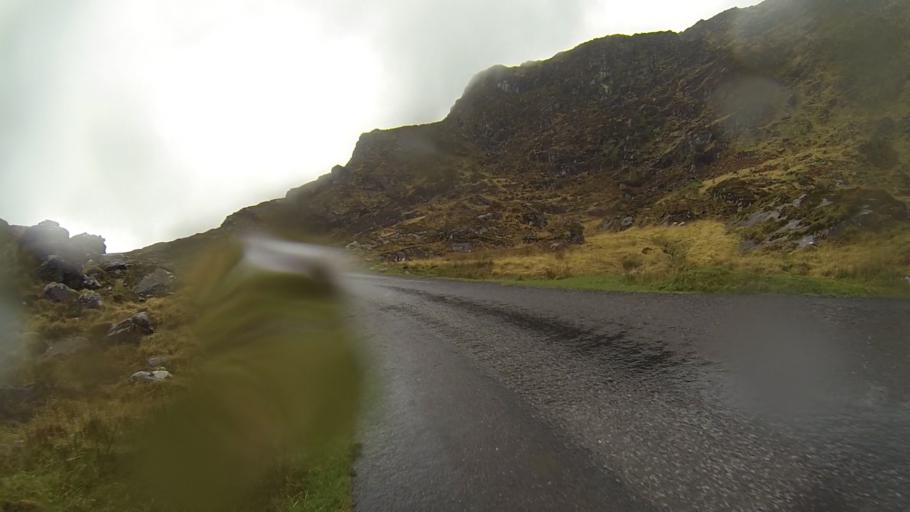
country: IE
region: Munster
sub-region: Ciarrai
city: Kenmare
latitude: 51.9968
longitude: -9.6441
